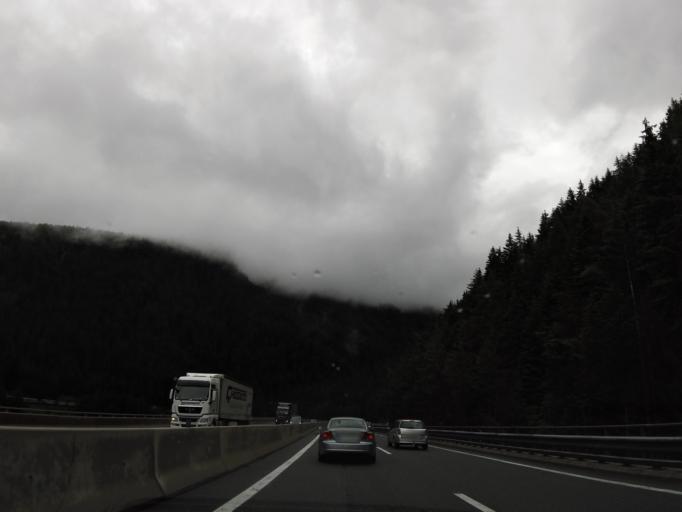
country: AT
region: Tyrol
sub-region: Politischer Bezirk Innsbruck Land
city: Gries am Brenner
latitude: 47.0259
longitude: 11.4955
